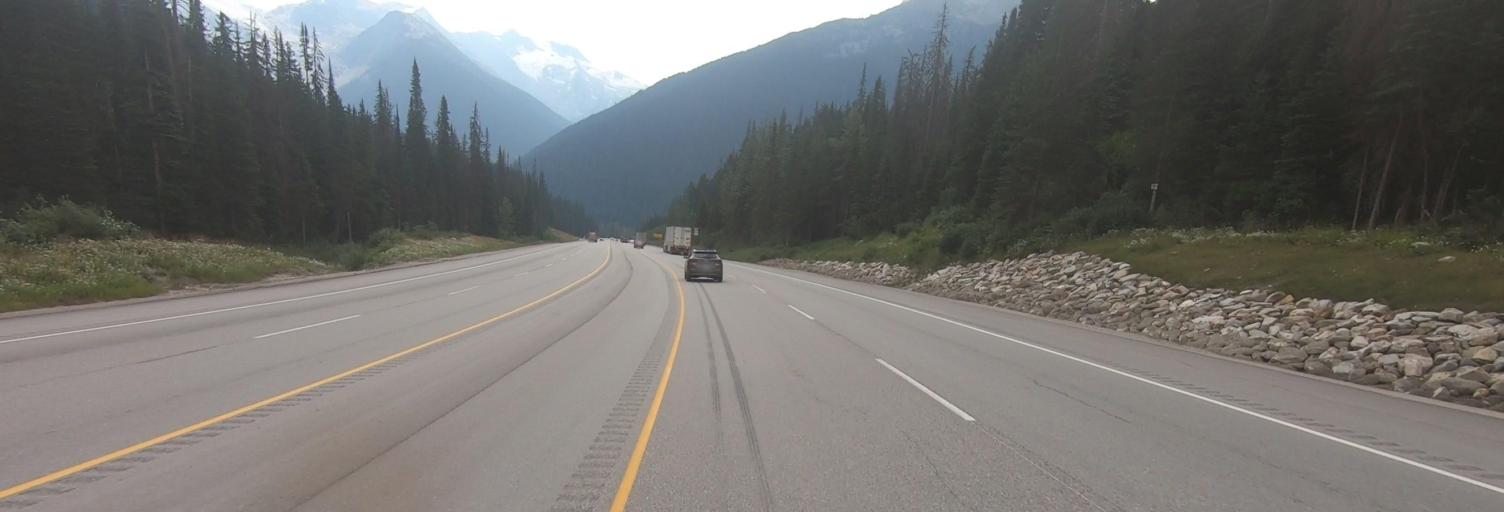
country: CA
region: British Columbia
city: Golden
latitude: 51.2822
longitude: -117.5135
